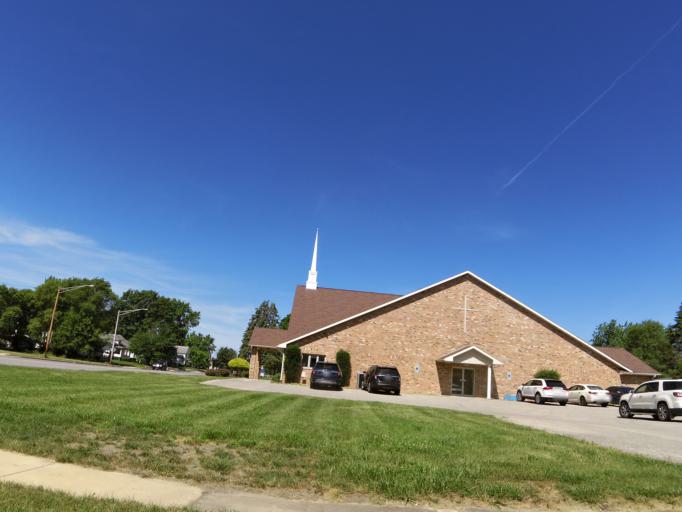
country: US
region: Illinois
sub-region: Vermilion County
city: Danville
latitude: 40.1324
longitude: -87.5820
